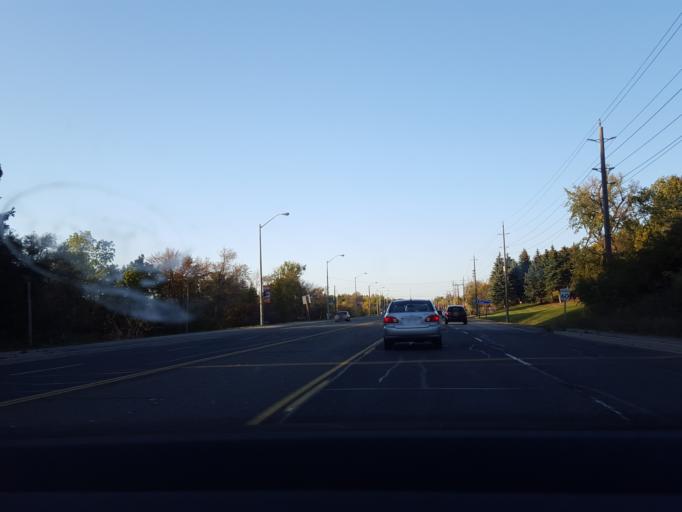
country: CA
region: Ontario
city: Newmarket
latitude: 44.0145
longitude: -79.4711
